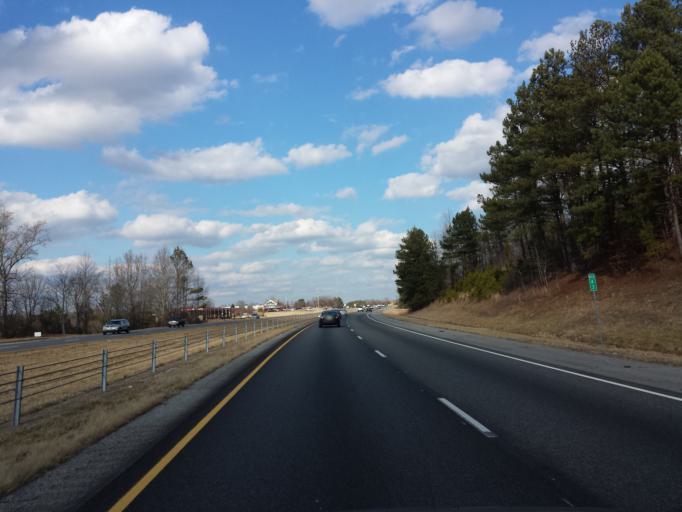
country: US
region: Georgia
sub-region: Dawson County
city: Dawsonville
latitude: 34.3413
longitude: -84.0538
